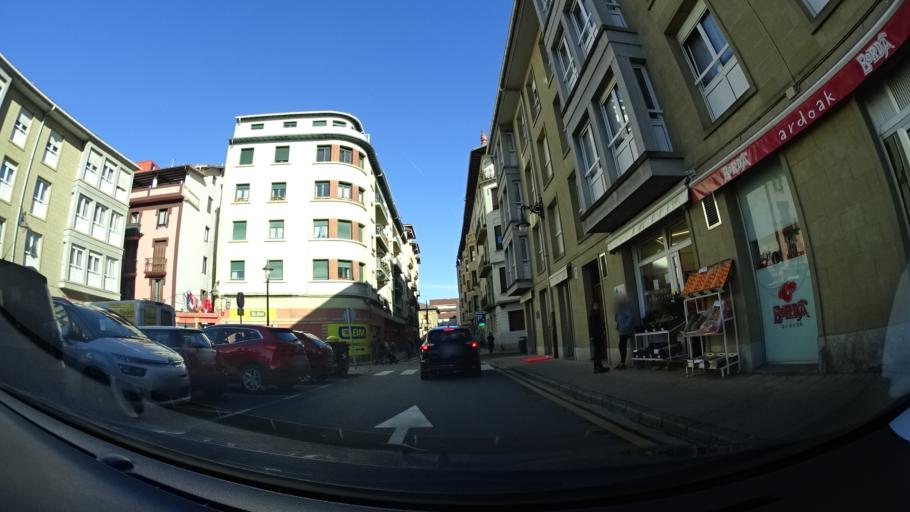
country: ES
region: Basque Country
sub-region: Provincia de Guipuzcoa
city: Zarautz
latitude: 43.2838
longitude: -2.1757
